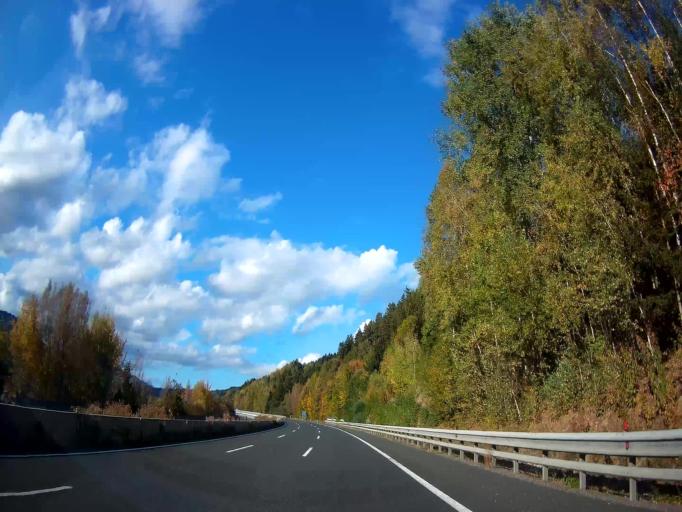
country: AT
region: Carinthia
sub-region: Politischer Bezirk Wolfsberg
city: Wolfsberg
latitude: 46.8666
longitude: 14.8364
